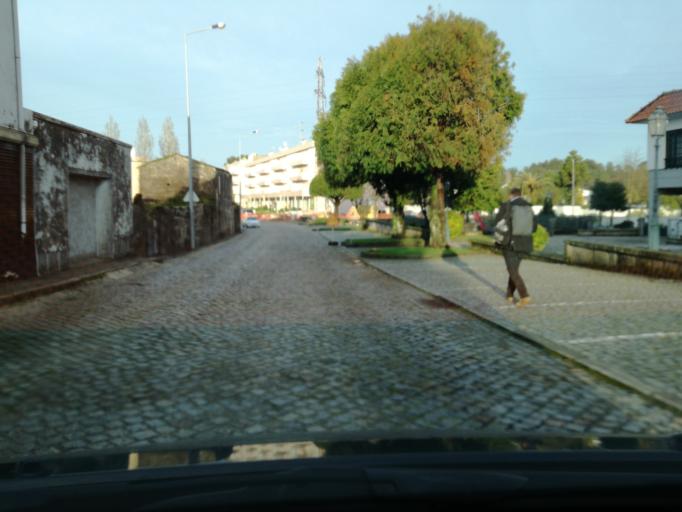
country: PT
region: Porto
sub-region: Maia
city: Anta
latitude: 41.2672
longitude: -8.6054
